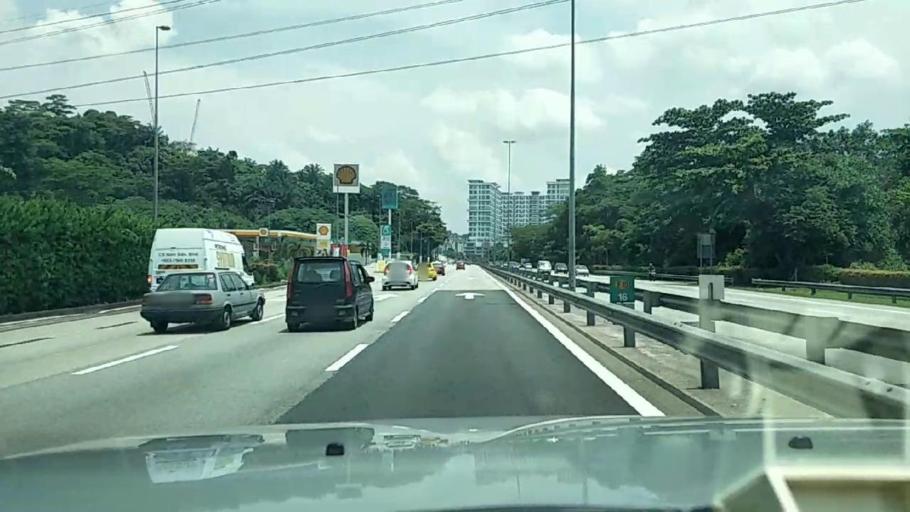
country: MY
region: Kuala Lumpur
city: Kuala Lumpur
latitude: 3.0941
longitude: 101.6822
